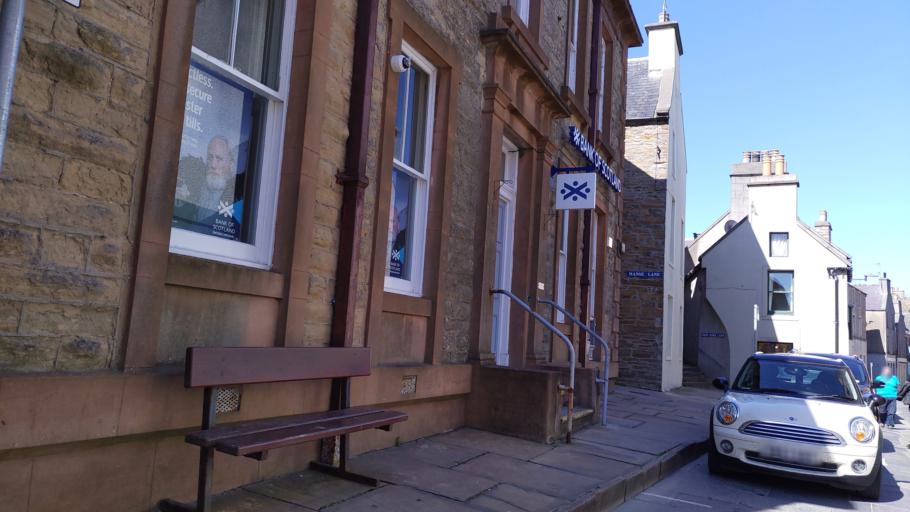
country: GB
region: Scotland
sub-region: Orkney Islands
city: Stromness
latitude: 58.9617
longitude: -3.2994
